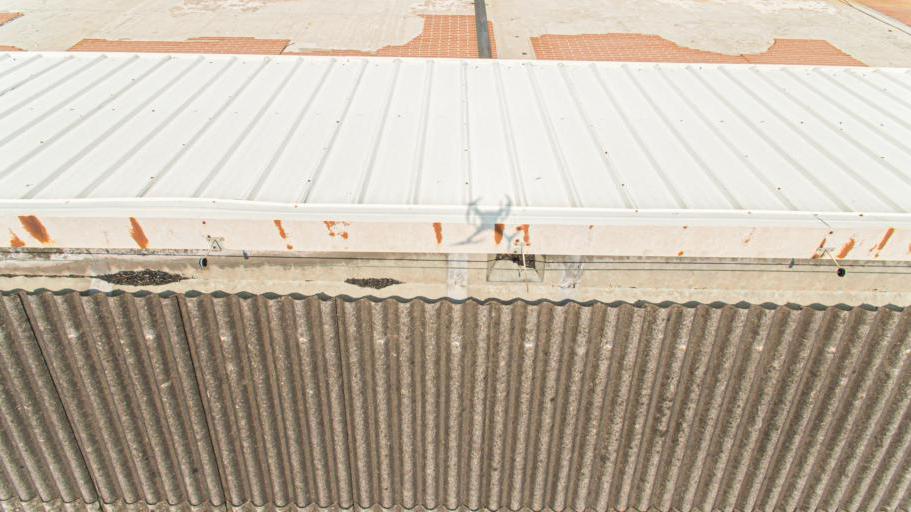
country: BR
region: Sao Paulo
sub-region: Cacapava
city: Cacapava
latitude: -23.1313
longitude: -45.7550
